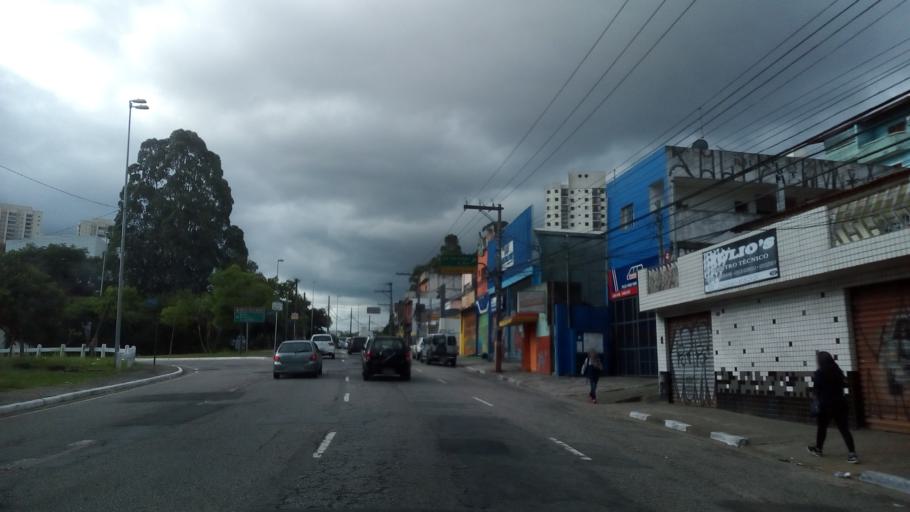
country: BR
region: Sao Paulo
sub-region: Guarulhos
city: Guarulhos
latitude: -23.4457
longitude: -46.5372
